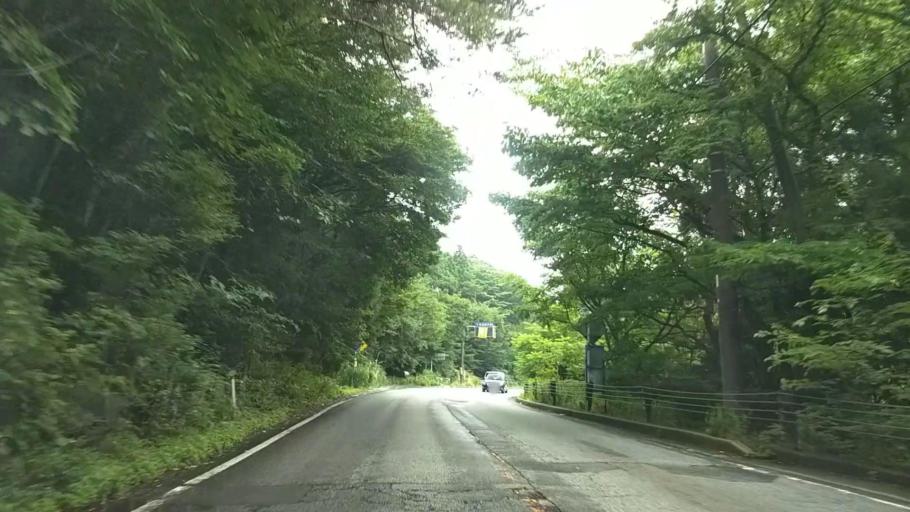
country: JP
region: Yamanashi
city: Fujikawaguchiko
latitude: 35.4554
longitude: 138.6088
